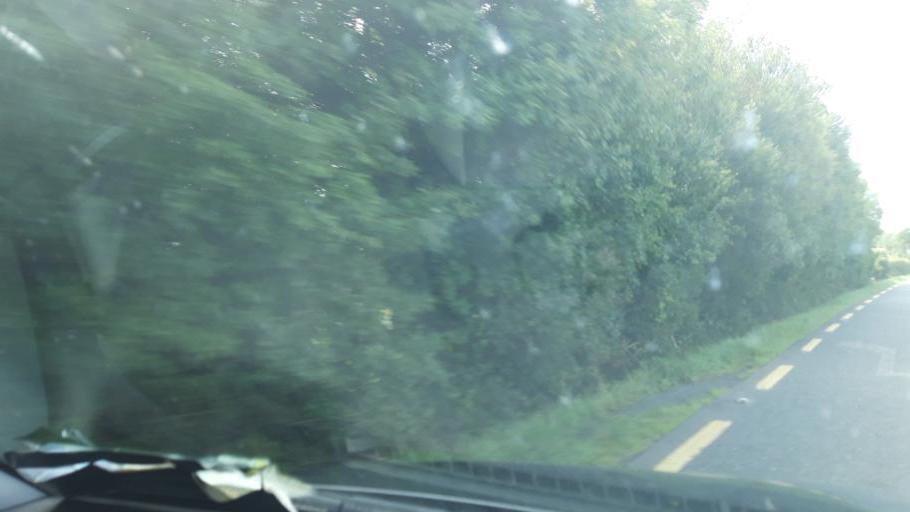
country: IE
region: Leinster
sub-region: Kilkenny
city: Callan
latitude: 52.5249
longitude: -7.4164
